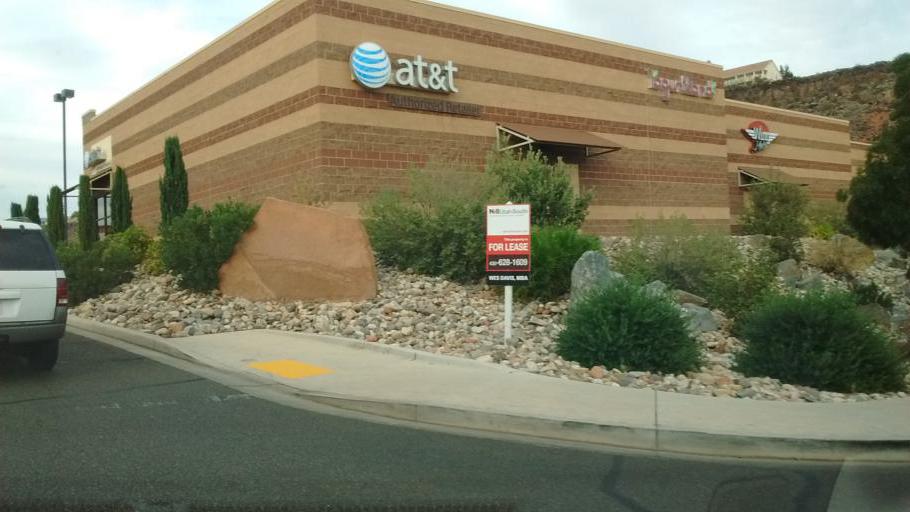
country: US
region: Utah
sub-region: Washington County
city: Saint George
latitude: 37.1064
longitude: -113.5545
